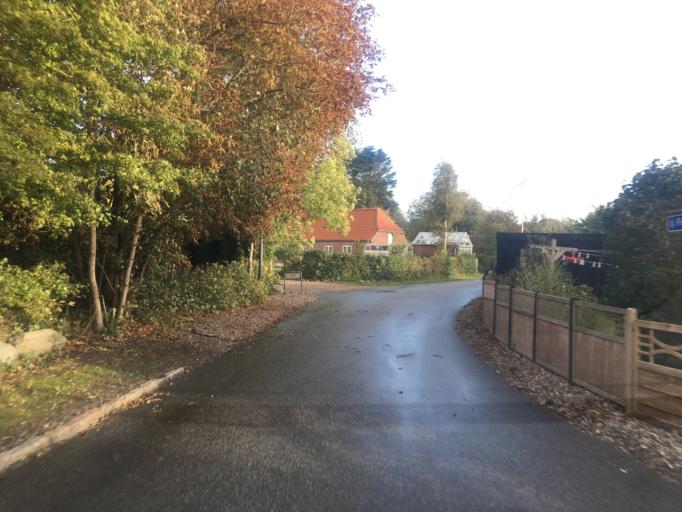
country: DE
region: Schleswig-Holstein
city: Aventoft
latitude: 54.9385
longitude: 8.8036
